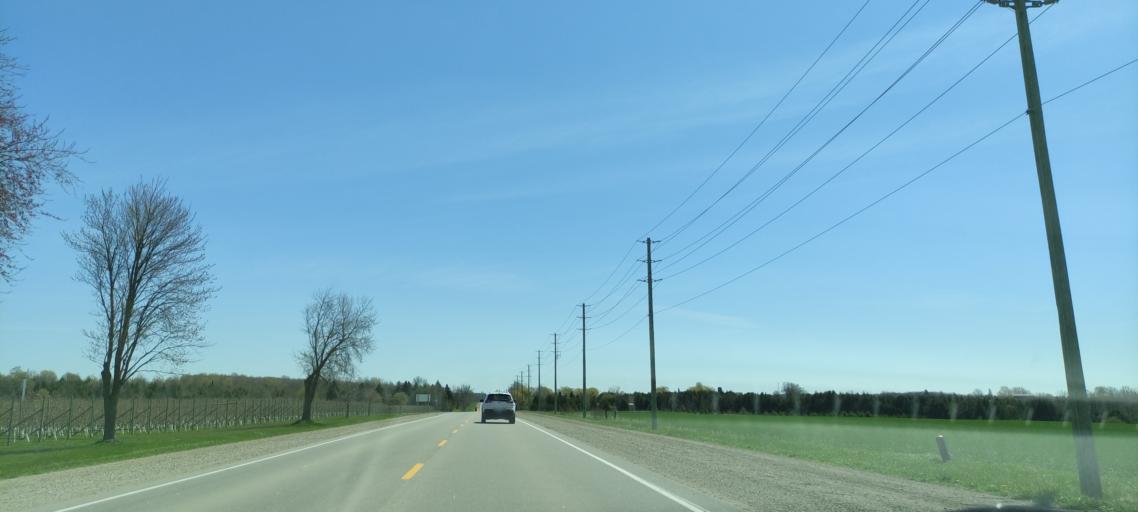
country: CA
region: Ontario
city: Waterloo
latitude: 43.5947
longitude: -80.5034
